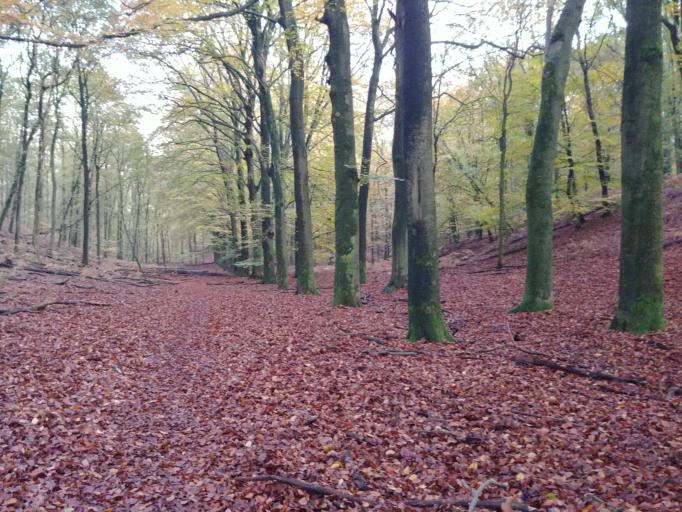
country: NL
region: Gelderland
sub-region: Gemeente Rheden
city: De Steeg
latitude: 52.0410
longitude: 6.0420
